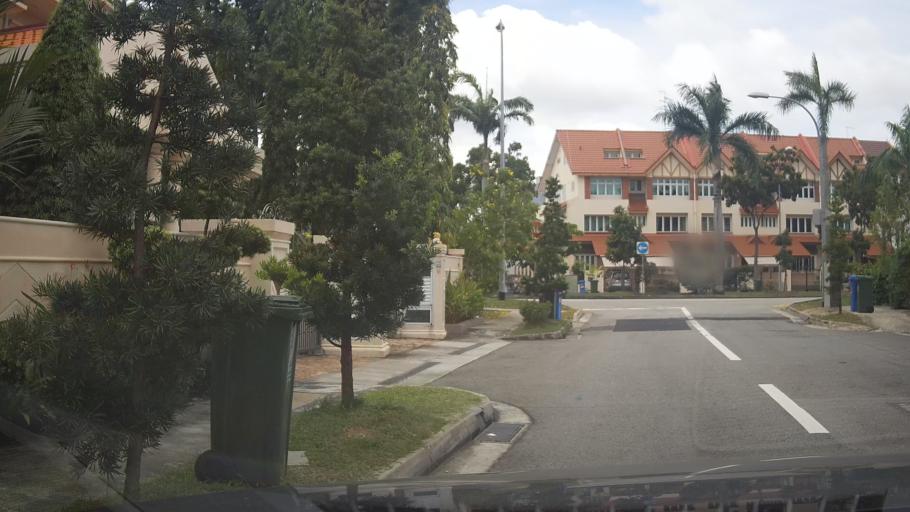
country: SG
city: Singapore
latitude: 1.3106
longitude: 103.9083
